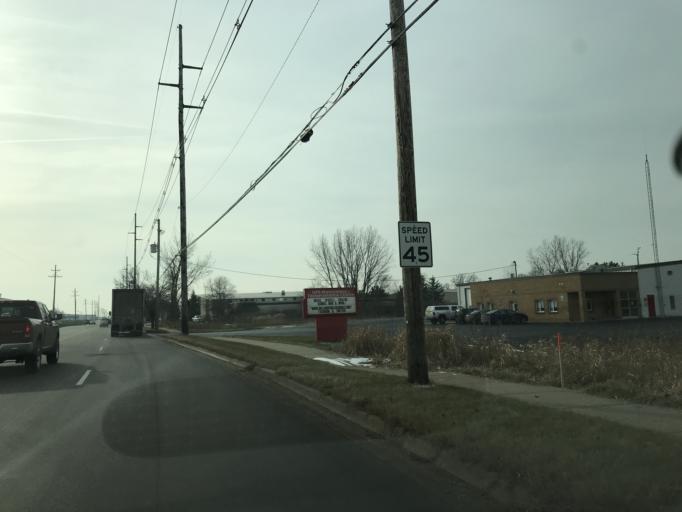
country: US
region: Michigan
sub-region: Ottawa County
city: Holland
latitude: 42.7674
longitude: -86.0778
